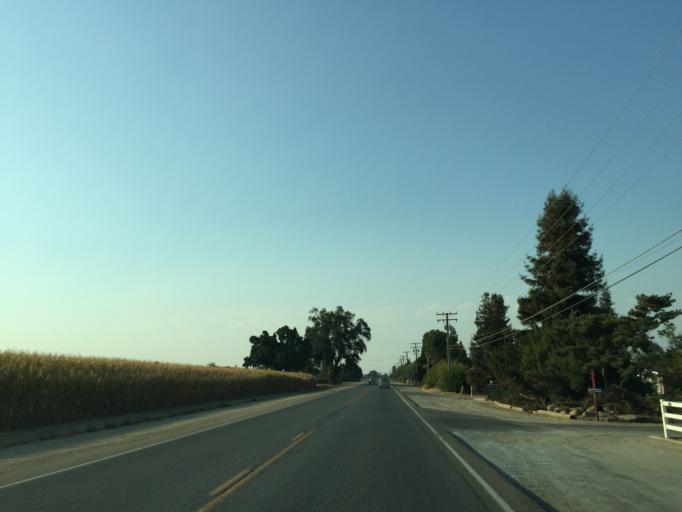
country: US
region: California
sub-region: Tulare County
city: Visalia
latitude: 36.3599
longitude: -119.2790
